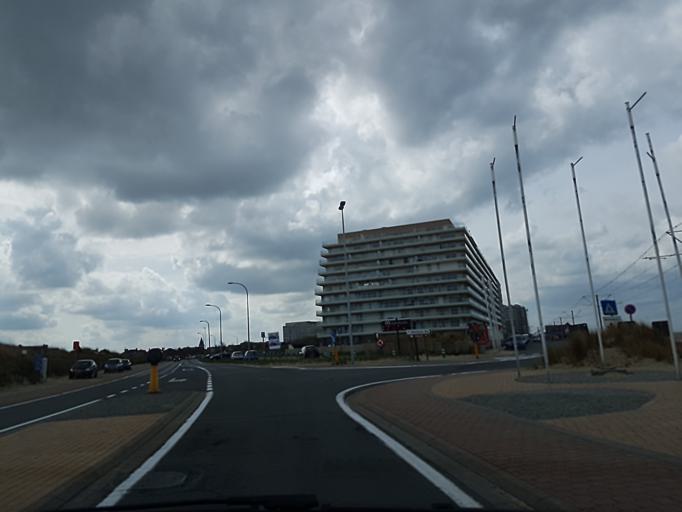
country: BE
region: Flanders
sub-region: Provincie West-Vlaanderen
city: Middelkerke
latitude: 51.1926
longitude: 2.8255
